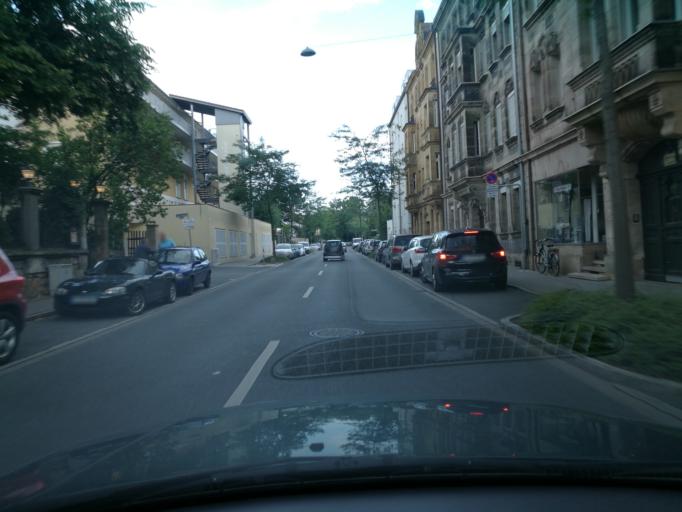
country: DE
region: Bavaria
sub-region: Regierungsbezirk Mittelfranken
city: Furth
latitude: 49.4817
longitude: 10.9770
